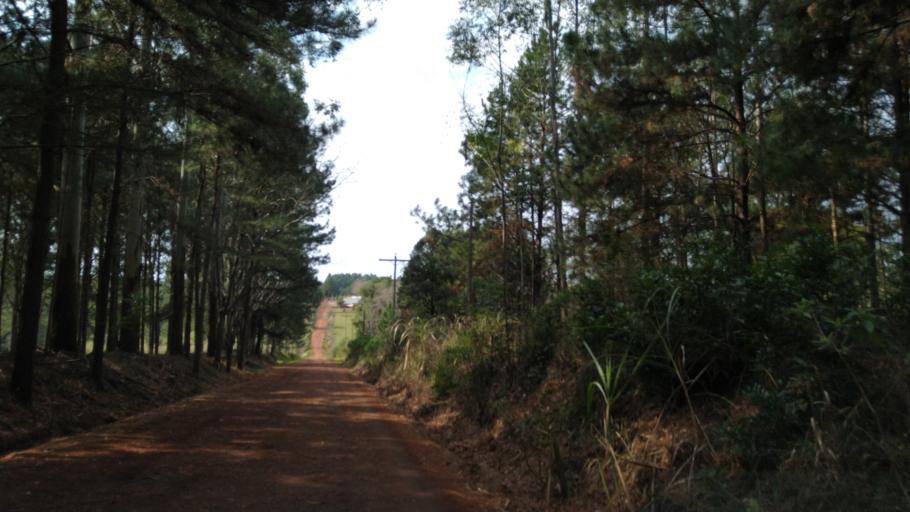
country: AR
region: Misiones
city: Capiovi
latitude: -26.9528
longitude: -55.0532
